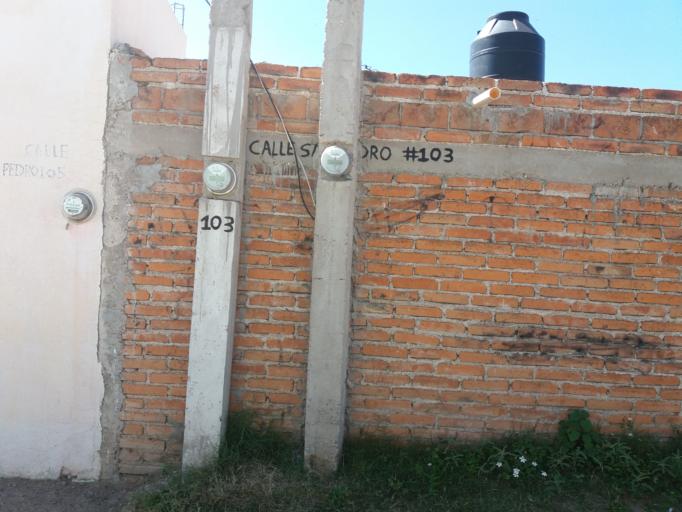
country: MX
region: Aguascalientes
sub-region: Aguascalientes
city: San Sebastian [Fraccionamiento]
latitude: 21.7797
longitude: -102.2290
